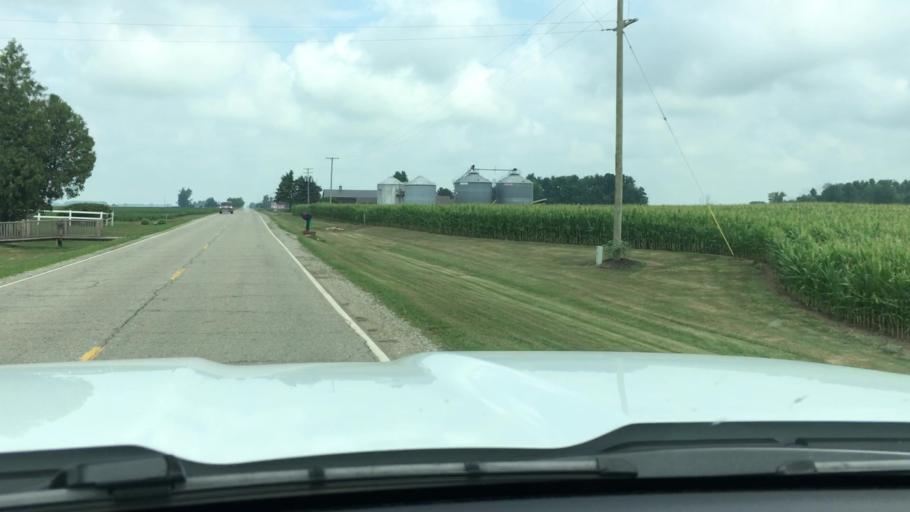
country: US
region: Michigan
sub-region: Sanilac County
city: Marlette
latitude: 43.3652
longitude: -83.0059
